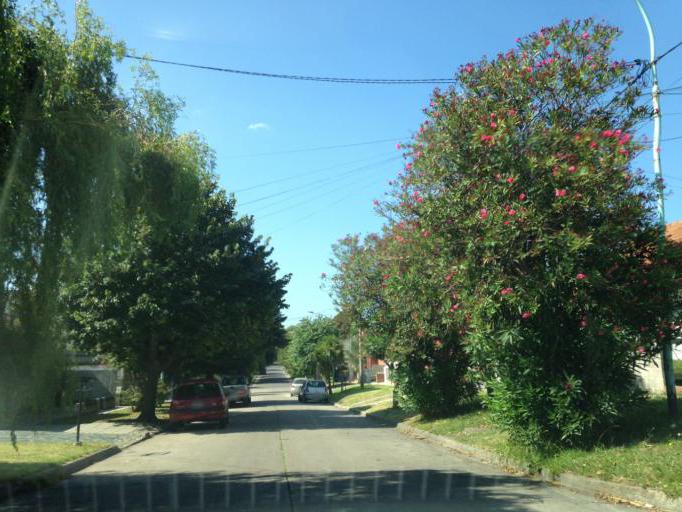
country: AR
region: Buenos Aires
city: Mar del Plata
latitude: -38.0334
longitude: -57.5489
